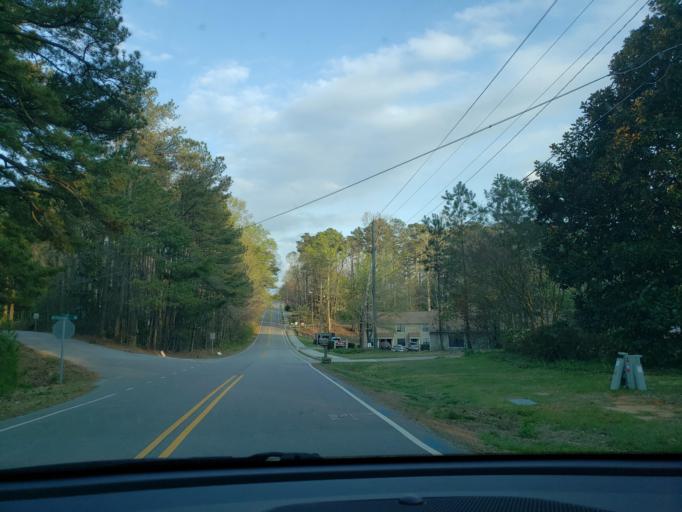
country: US
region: North Carolina
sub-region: Wake County
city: Apex
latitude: 35.7330
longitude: -78.8577
